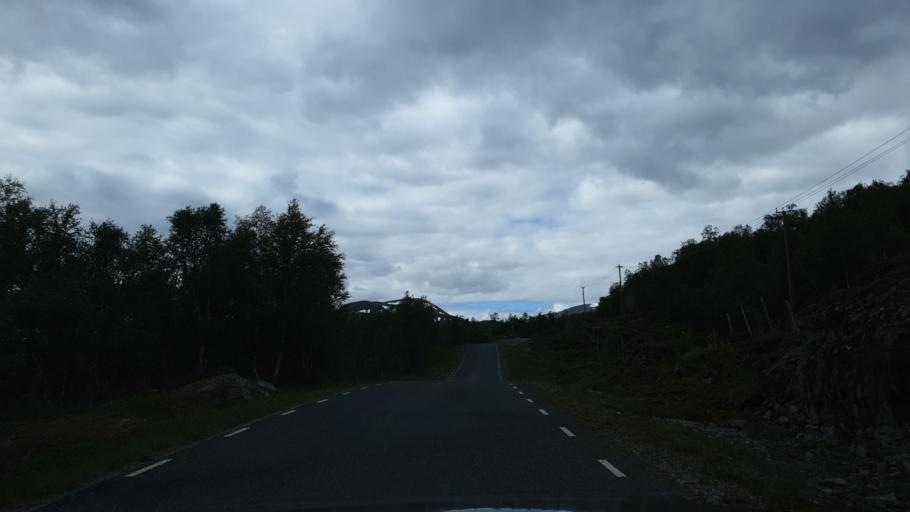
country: NO
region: Nordland
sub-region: Hattfjelldal
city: Hattfjelldal
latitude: 65.4169
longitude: 14.6862
